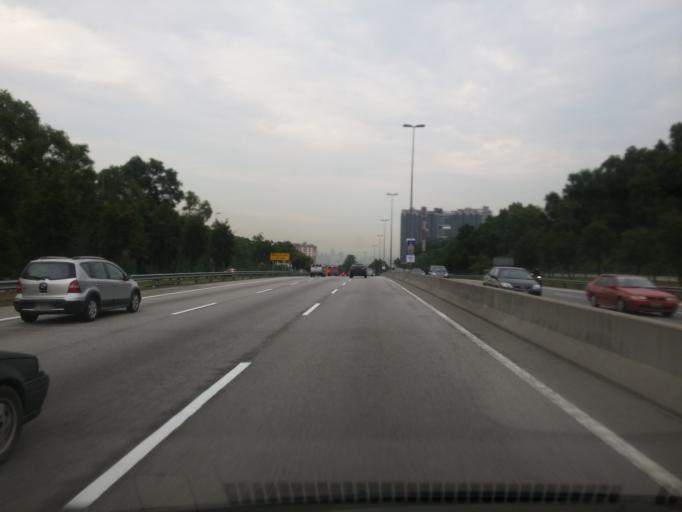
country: MY
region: Kuala Lumpur
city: Kuala Lumpur
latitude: 3.0793
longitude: 101.6913
